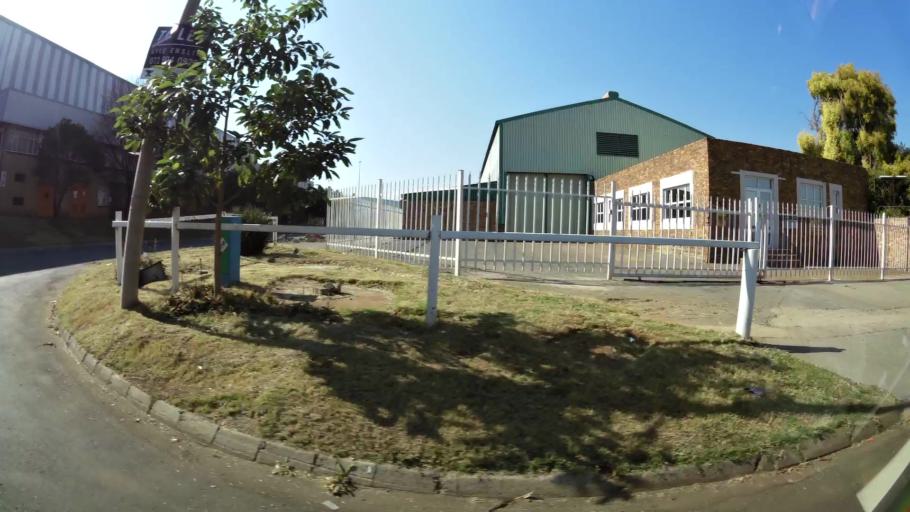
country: ZA
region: Gauteng
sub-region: Ekurhuleni Metropolitan Municipality
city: Boksburg
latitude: -26.1577
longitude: 28.2234
